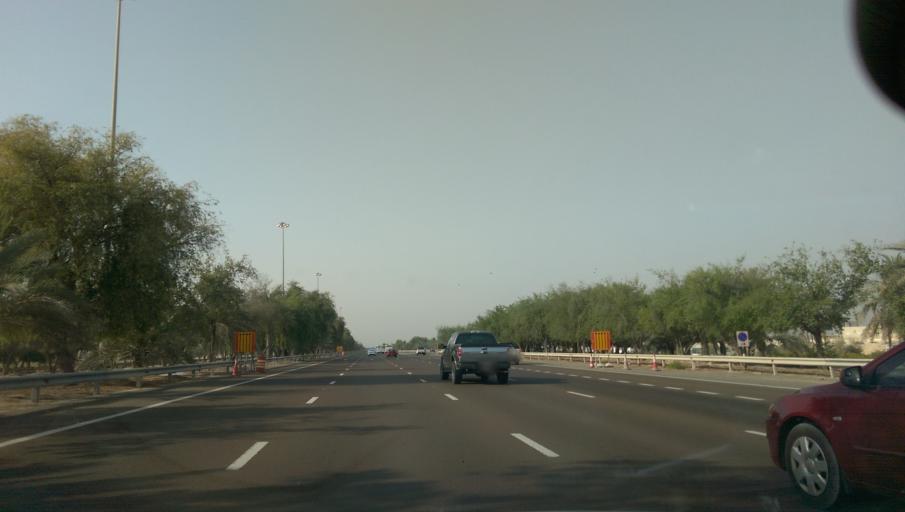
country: AE
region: Abu Dhabi
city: Abu Dhabi
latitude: 24.4451
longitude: 54.6785
